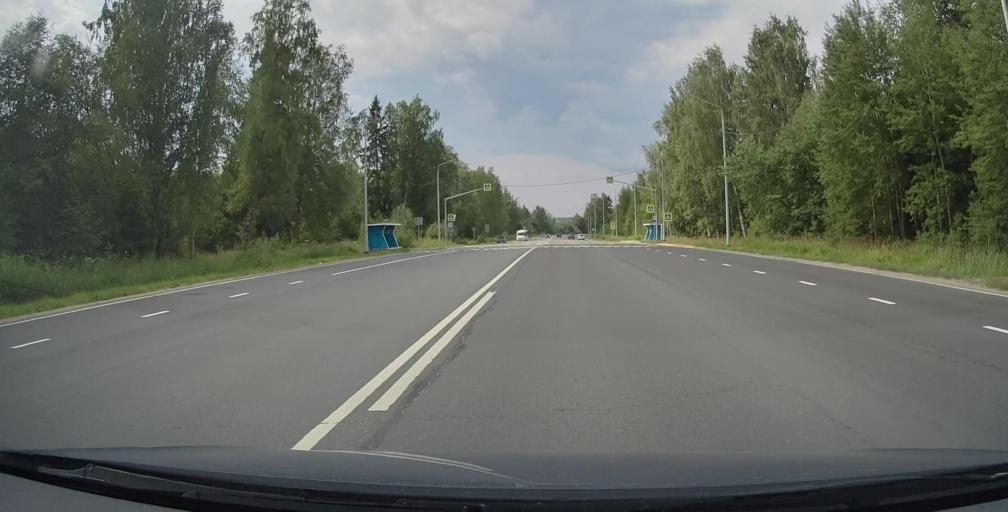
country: RU
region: Jaroslavl
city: Tutayev
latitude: 57.8839
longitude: 39.4481
